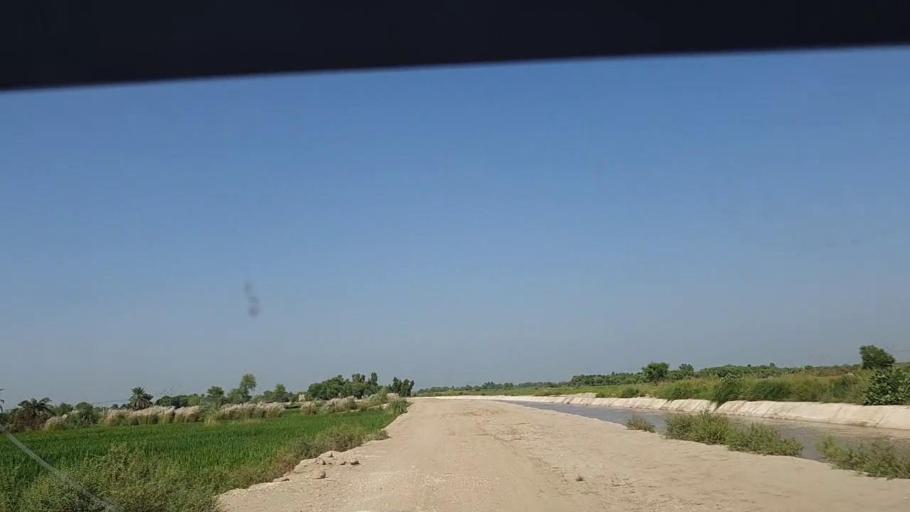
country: PK
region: Sindh
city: Ghauspur
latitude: 28.1613
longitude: 69.0939
